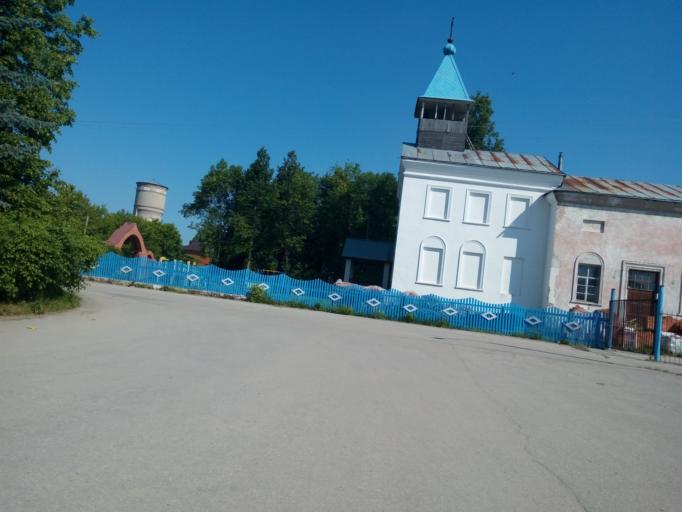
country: RU
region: Nizjnij Novgorod
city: Voskresenskoye
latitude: 56.8359
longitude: 45.4381
